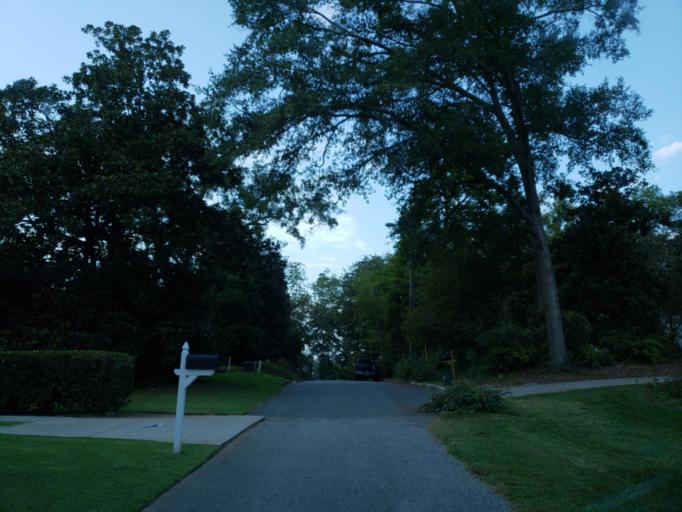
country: US
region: Georgia
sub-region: Cobb County
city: Marietta
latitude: 33.9481
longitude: -84.5555
